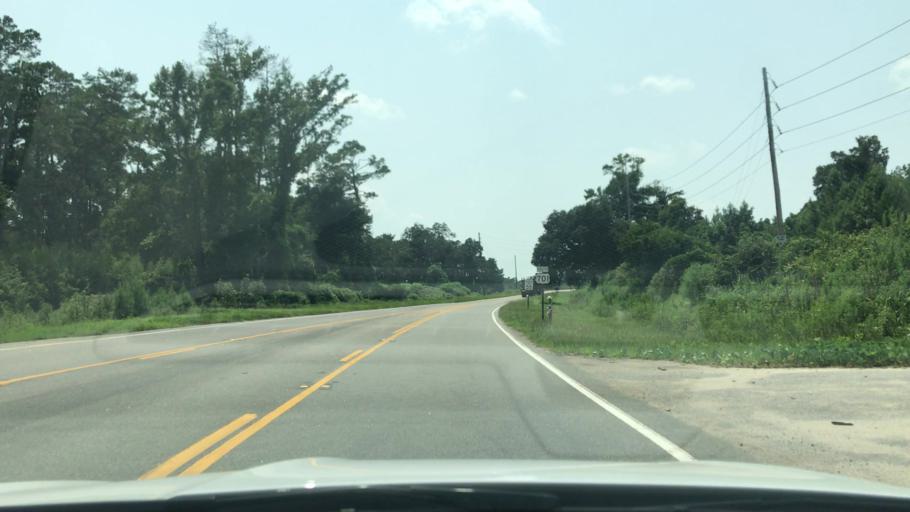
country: US
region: South Carolina
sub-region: Georgetown County
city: Georgetown
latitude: 33.4818
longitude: -79.2700
